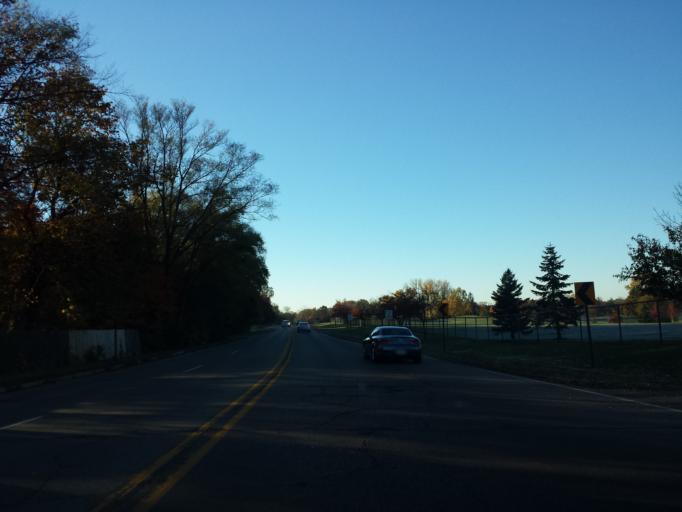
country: US
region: Michigan
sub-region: Oakland County
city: Beverly Hills
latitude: 42.5370
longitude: -83.2459
